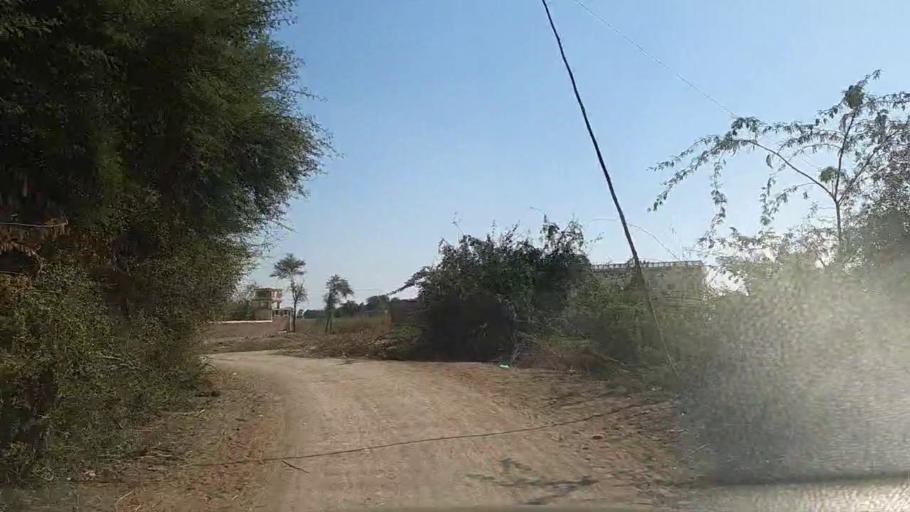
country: PK
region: Sindh
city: Nawabshah
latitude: 26.2377
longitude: 68.4493
